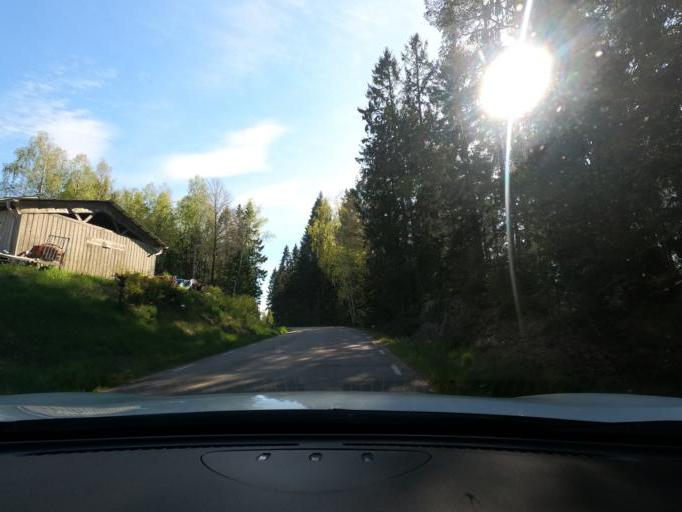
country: SE
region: Vaestra Goetaland
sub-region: Harryda Kommun
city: Hindas
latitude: 57.6496
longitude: 12.3581
